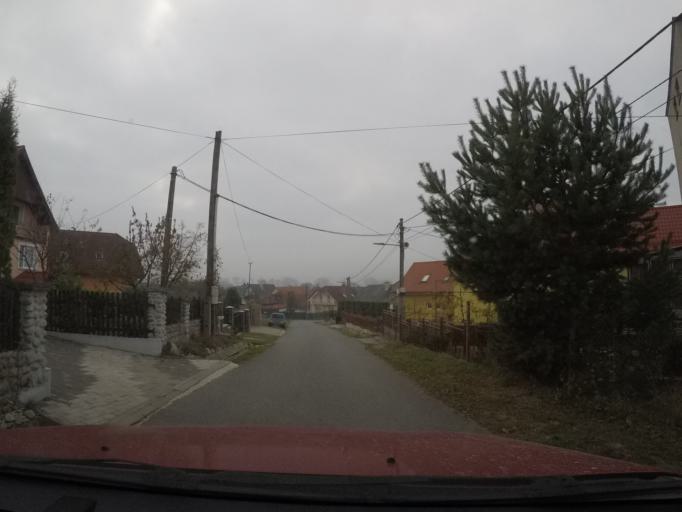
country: SK
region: Presovsky
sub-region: Okres Presov
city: Presov
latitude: 48.8756
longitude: 21.2677
